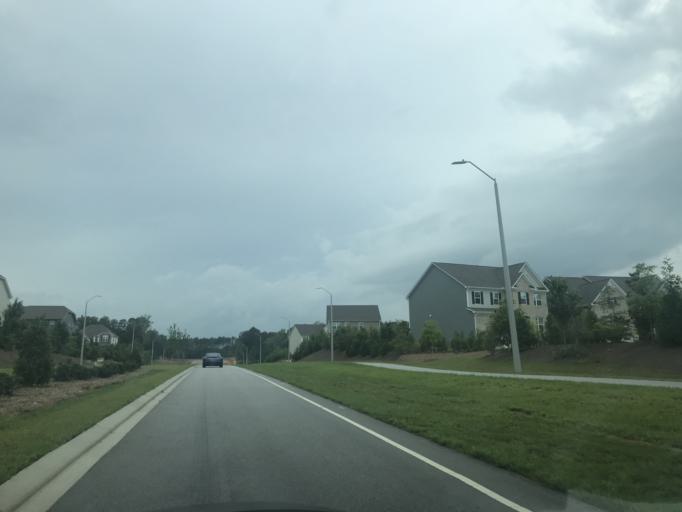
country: US
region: North Carolina
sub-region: Wake County
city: Green Level
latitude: 35.8108
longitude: -78.8834
